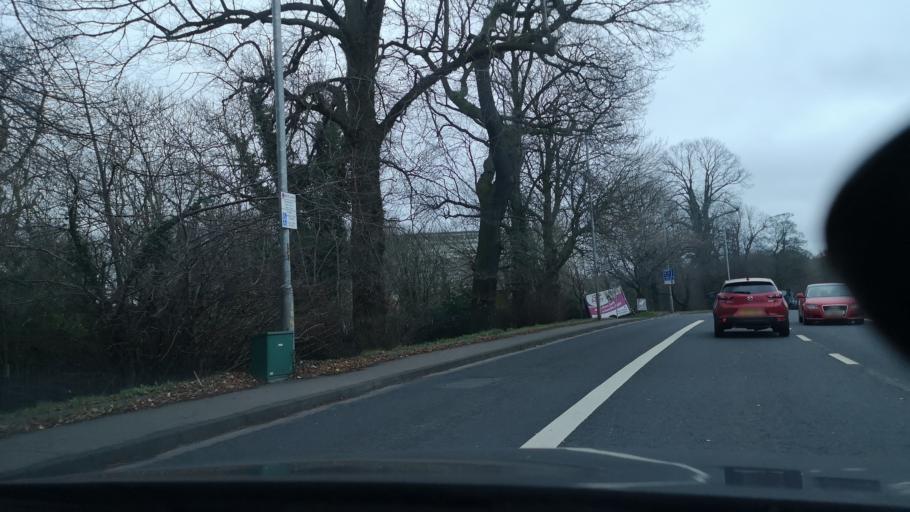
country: GB
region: Northern Ireland
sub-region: Castlereagh District
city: Dundonald
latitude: 54.5949
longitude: -5.8308
